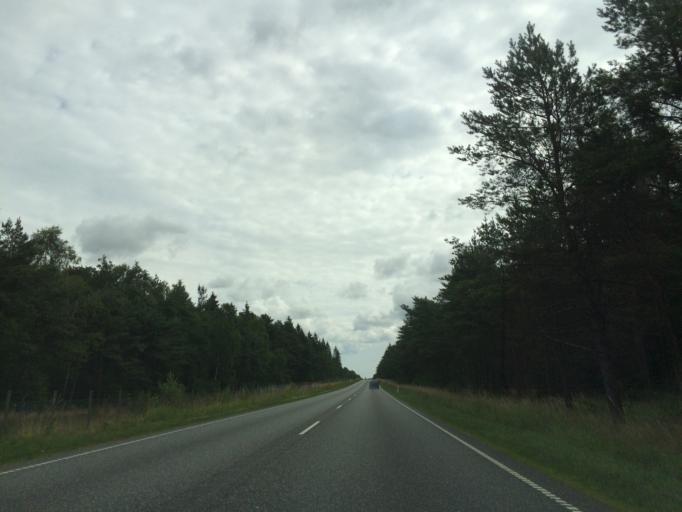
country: DK
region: Central Jutland
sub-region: Syddjurs Kommune
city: Ebeltoft
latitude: 56.2935
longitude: 10.6230
